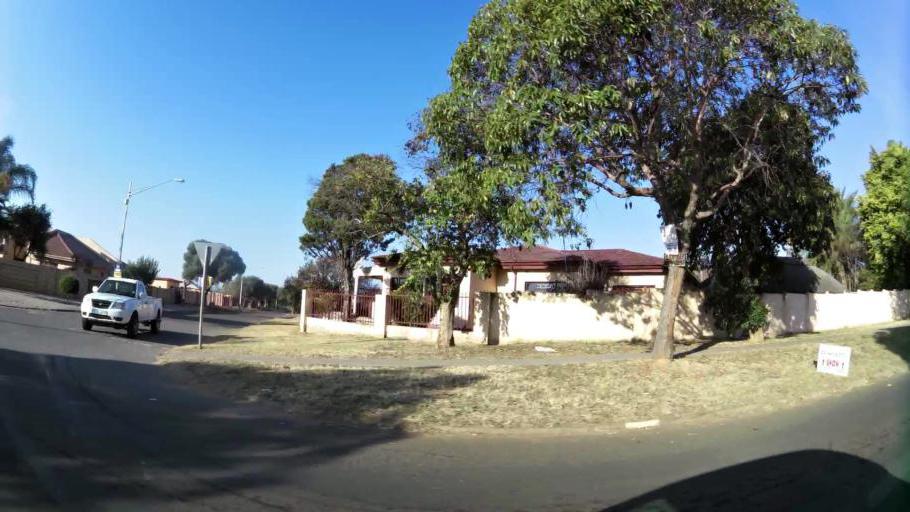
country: ZA
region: Gauteng
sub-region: City of Tshwane Metropolitan Municipality
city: Pretoria
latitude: -25.7525
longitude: 28.1206
